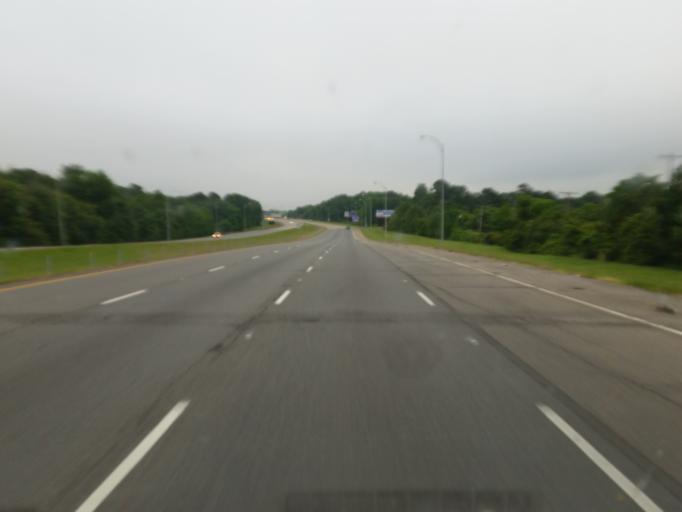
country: US
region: Louisiana
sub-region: Caddo Parish
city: Shreveport
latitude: 32.4625
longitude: -93.8240
